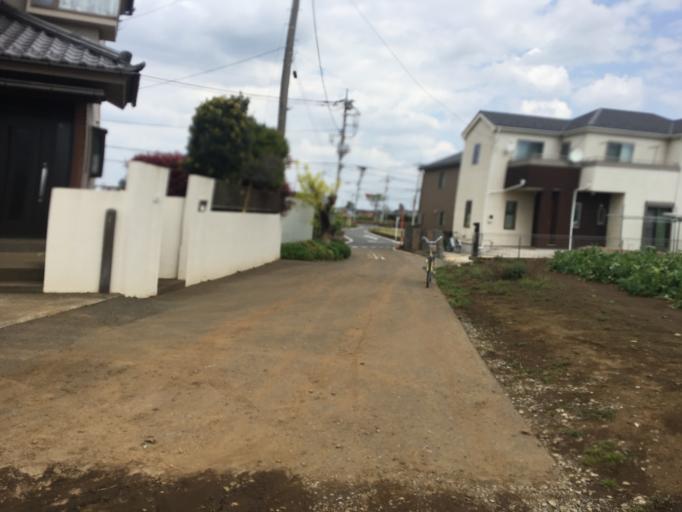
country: JP
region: Saitama
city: Oi
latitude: 35.8293
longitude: 139.5466
